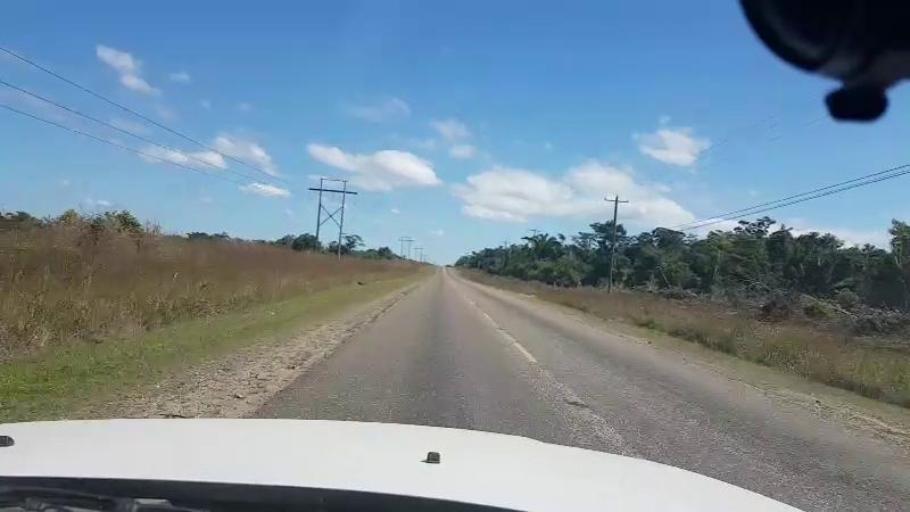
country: BZ
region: Cayo
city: Belmopan
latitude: 17.2767
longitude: -88.7360
